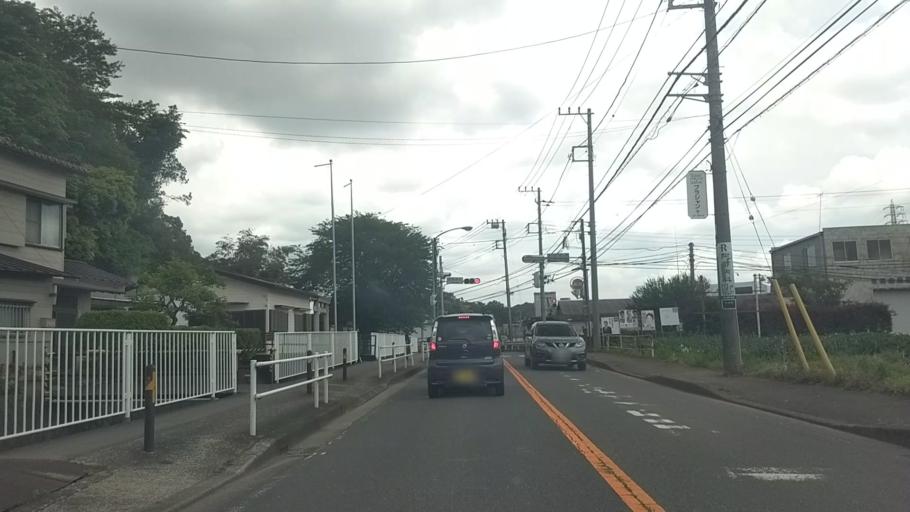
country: JP
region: Kanagawa
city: Fujisawa
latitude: 35.3683
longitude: 139.5223
